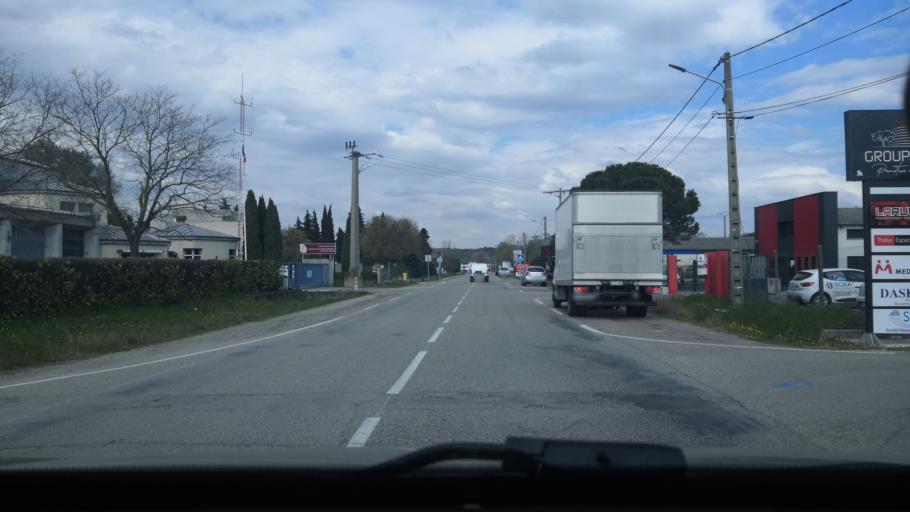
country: FR
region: Rhone-Alpes
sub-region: Departement de la Drome
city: Montelimar
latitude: 44.5749
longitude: 4.7472
